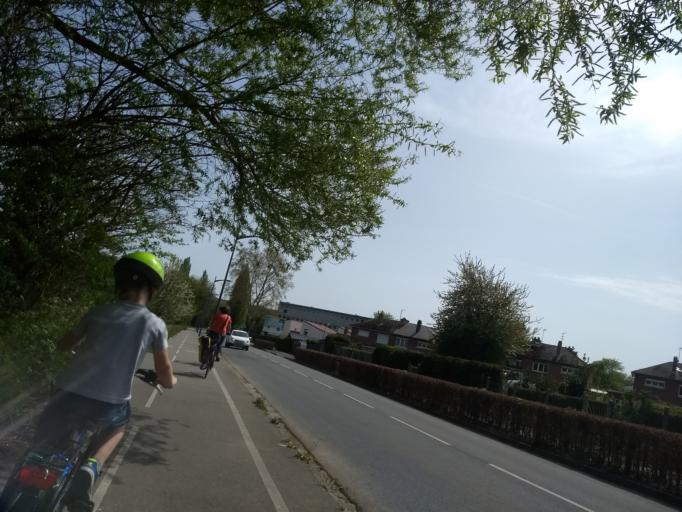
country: FR
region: Nord-Pas-de-Calais
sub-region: Departement du Pas-de-Calais
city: Anzin-Saint-Aubin
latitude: 50.3034
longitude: 2.7496
